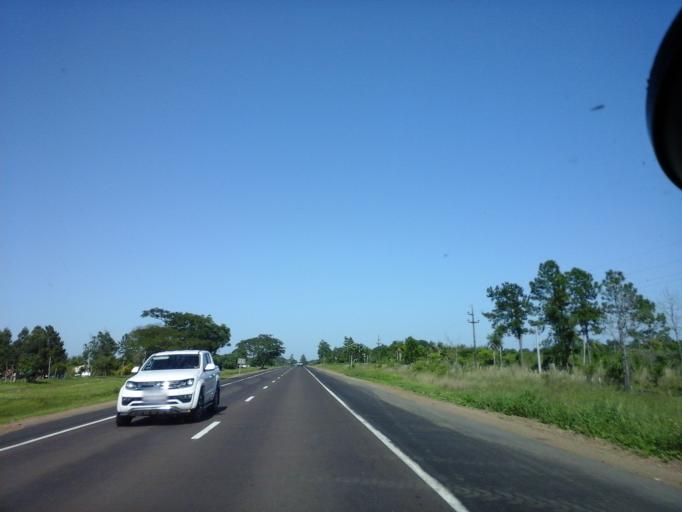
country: AR
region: Corrientes
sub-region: Departamento de Itati
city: Itati
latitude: -27.3669
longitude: -58.3472
